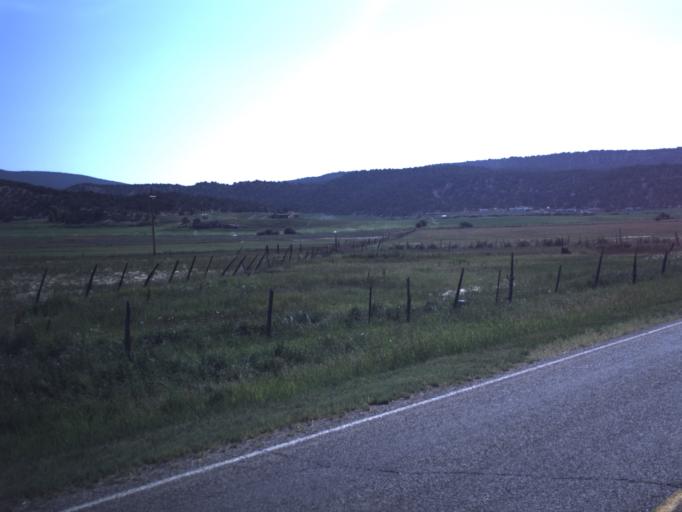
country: US
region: Utah
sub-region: Duchesne County
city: Duchesne
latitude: 40.3387
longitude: -110.6867
